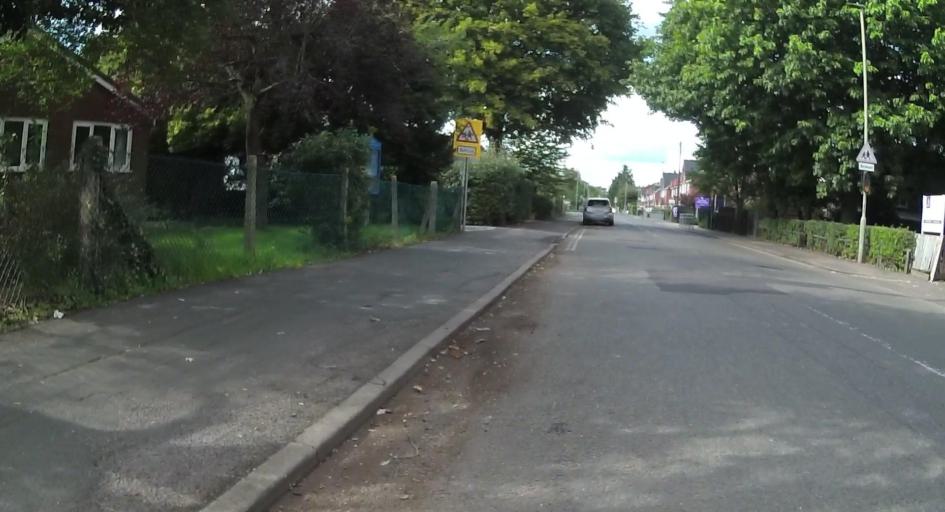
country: GB
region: England
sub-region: Surrey
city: Walton-on-Thames
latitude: 51.3824
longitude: -0.4000
